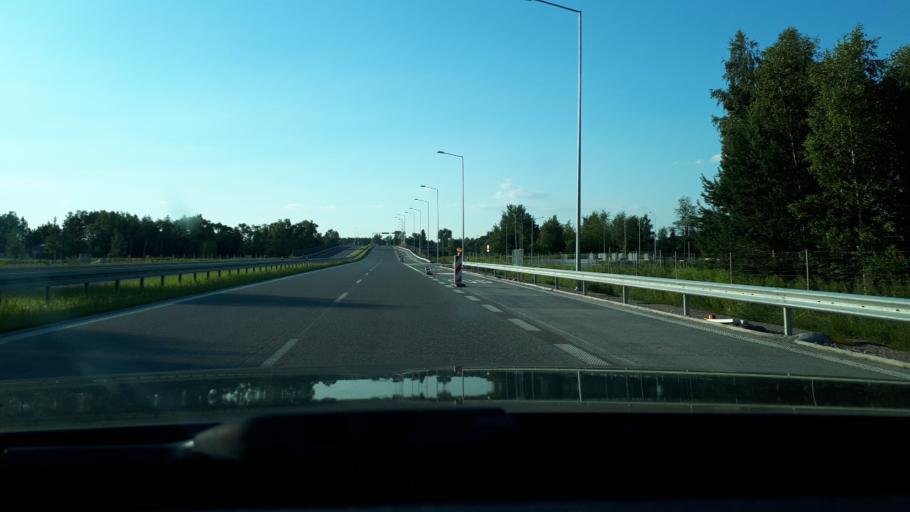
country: PL
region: Masovian Voivodeship
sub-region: Powiat piaseczynski
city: Baniocha
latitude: 51.9974
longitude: 21.1690
